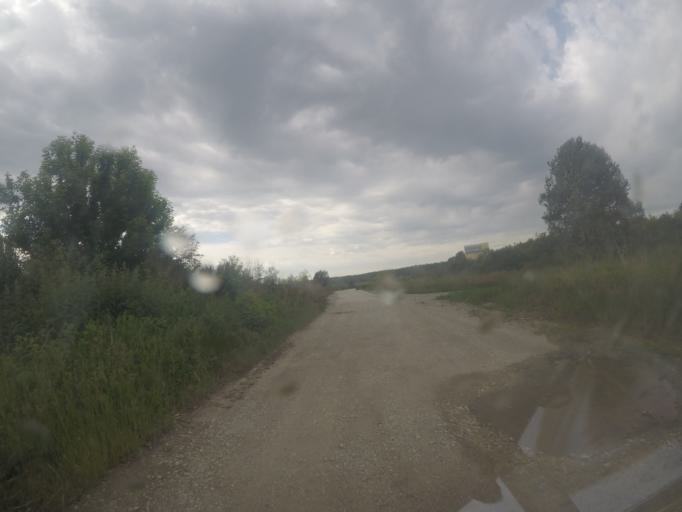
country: RS
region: Central Serbia
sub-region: Belgrade
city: Zemun
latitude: 44.8802
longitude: 20.3836
